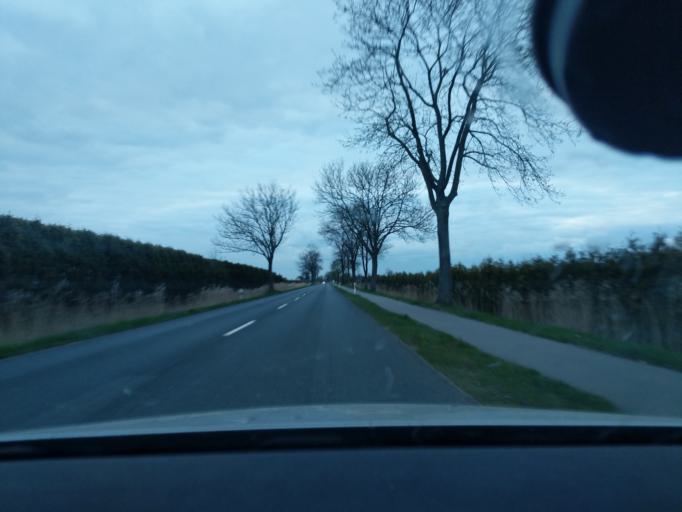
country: DE
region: Lower Saxony
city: Jork
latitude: 53.5237
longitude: 9.7537
